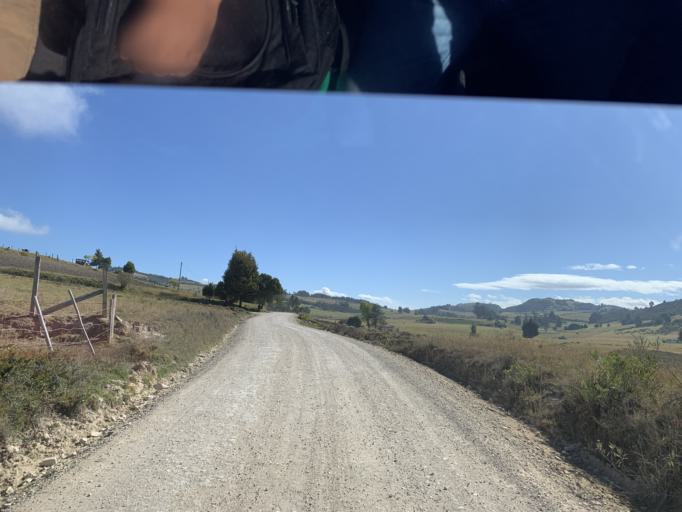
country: CO
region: Boyaca
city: Tuta
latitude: 5.6743
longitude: -73.1476
